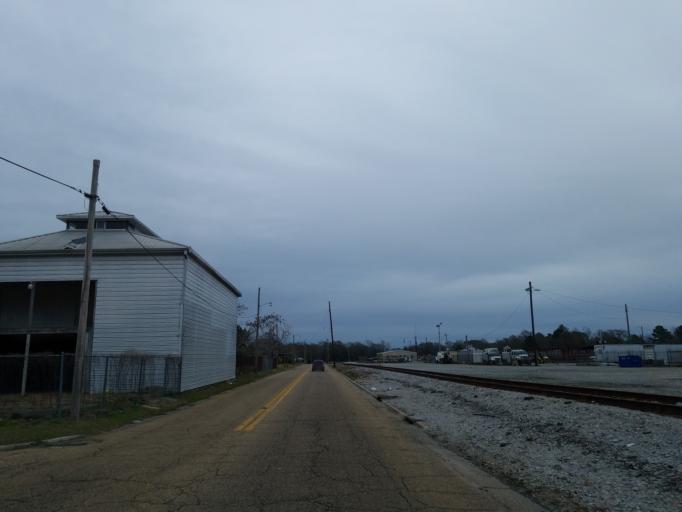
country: US
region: Mississippi
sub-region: Forrest County
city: Hattiesburg
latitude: 31.3287
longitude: -89.2870
